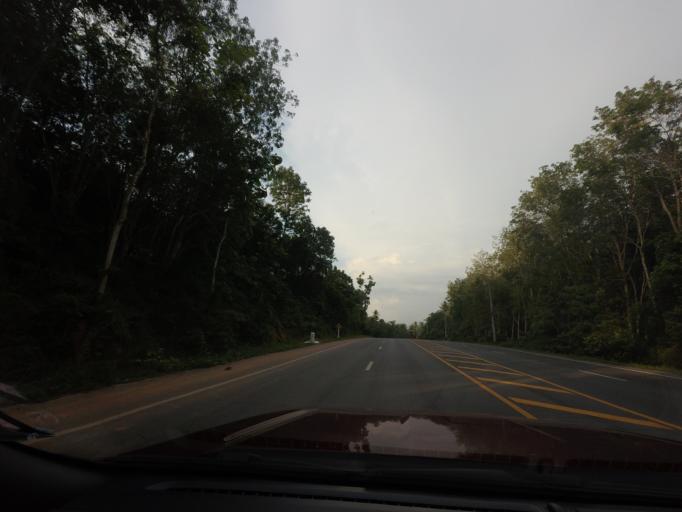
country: TH
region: Pattani
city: Khok Pho
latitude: 6.6768
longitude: 101.1199
